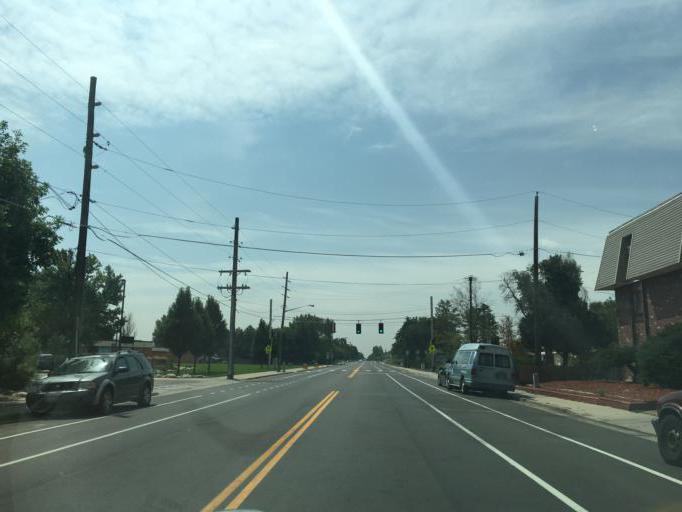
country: US
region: Colorado
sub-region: Adams County
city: Aurora
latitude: 39.7383
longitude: -104.8006
